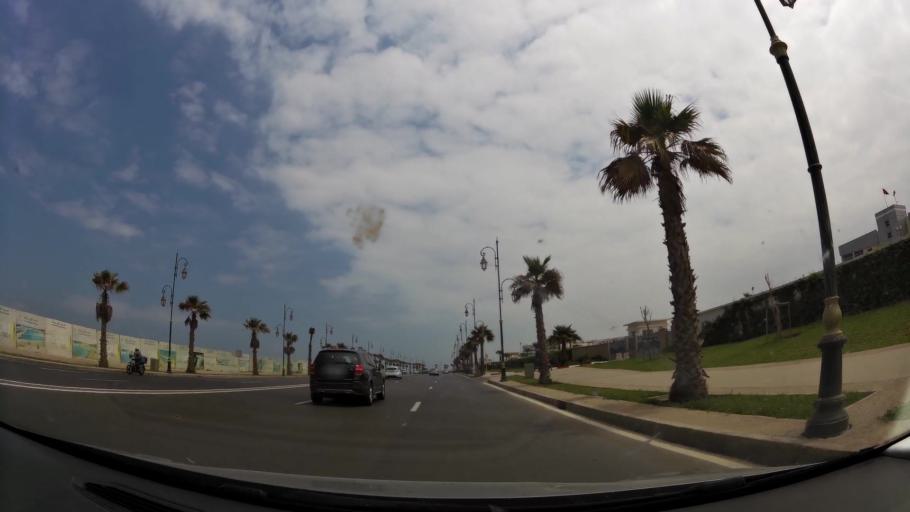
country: MA
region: Rabat-Sale-Zemmour-Zaer
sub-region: Rabat
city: Rabat
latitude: 33.9891
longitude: -6.8868
